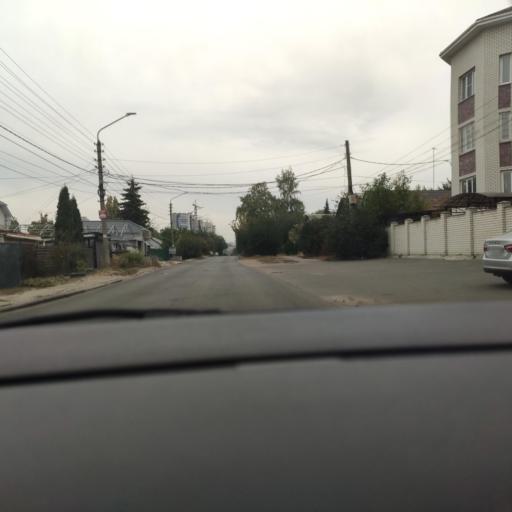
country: RU
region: Voronezj
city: Voronezh
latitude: 51.6926
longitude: 39.1704
